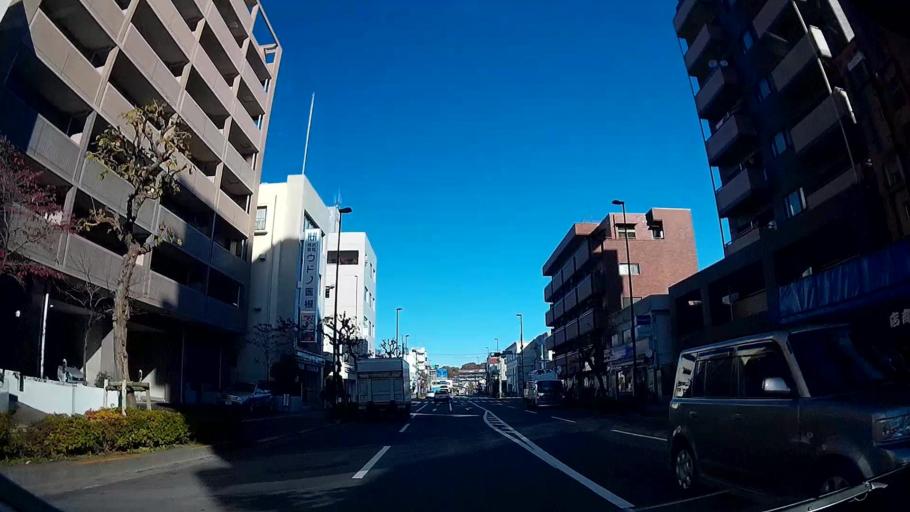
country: JP
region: Tokyo
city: Hachioji
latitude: 35.6612
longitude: 139.3396
